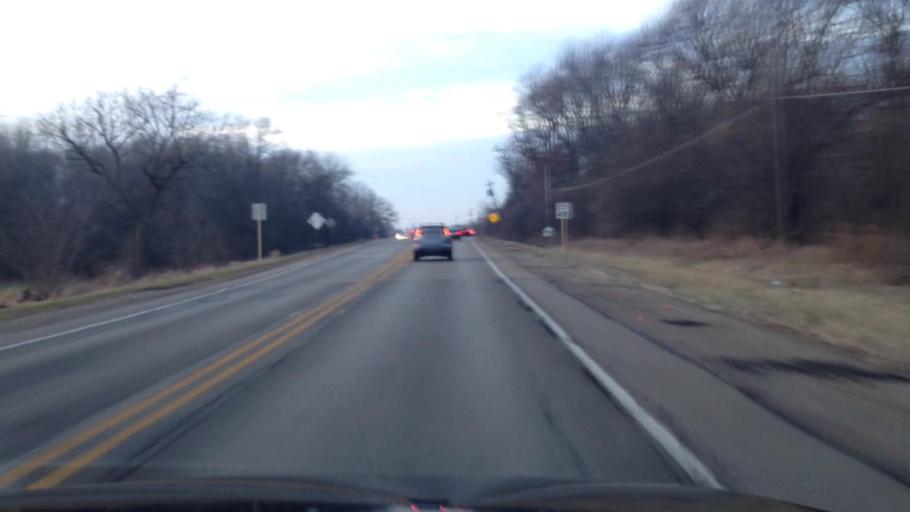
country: US
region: Illinois
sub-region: Kane County
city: Carpentersville
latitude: 42.1488
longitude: -88.2534
